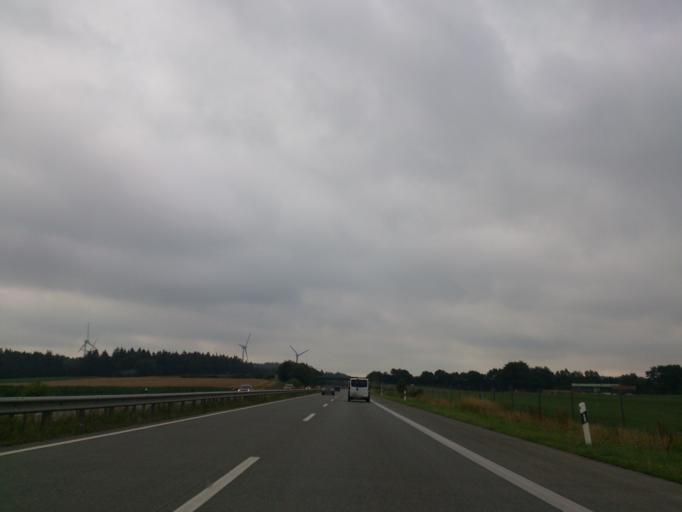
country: DE
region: Schleswig-Holstein
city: Bokelrehm
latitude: 54.0511
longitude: 9.3897
